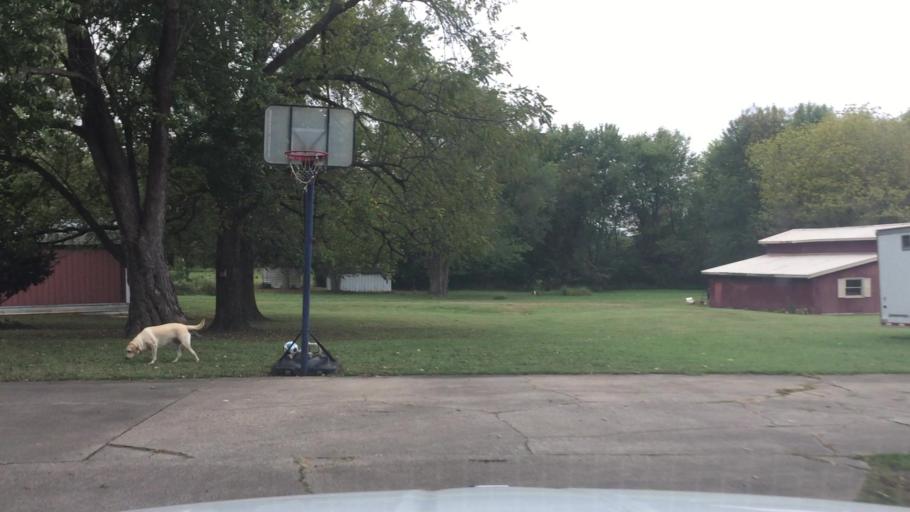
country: US
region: Illinois
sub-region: Franklin County
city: West Frankfort
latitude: 37.8989
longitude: -88.9727
